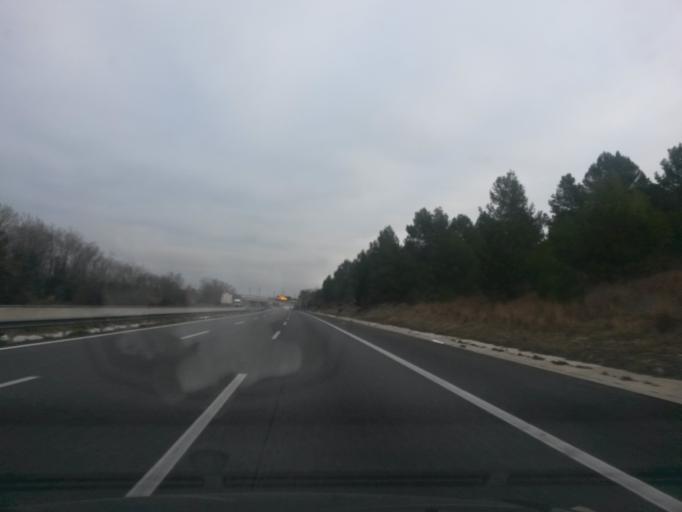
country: ES
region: Catalonia
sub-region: Provincia de Girona
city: Pontos
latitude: 42.1840
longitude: 2.9334
